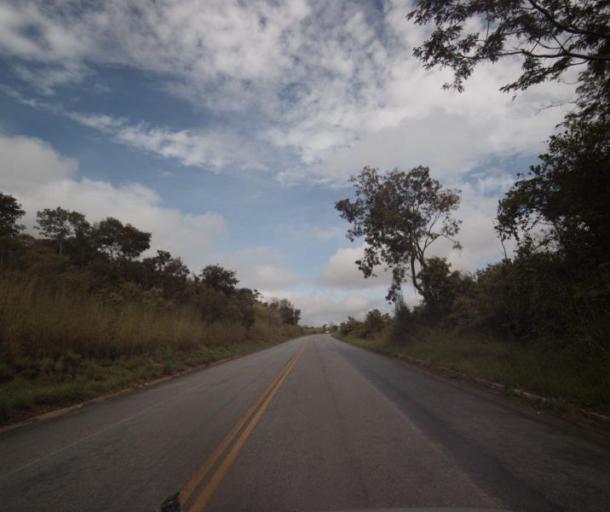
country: BR
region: Goias
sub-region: Pirenopolis
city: Pirenopolis
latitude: -15.7222
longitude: -48.6994
